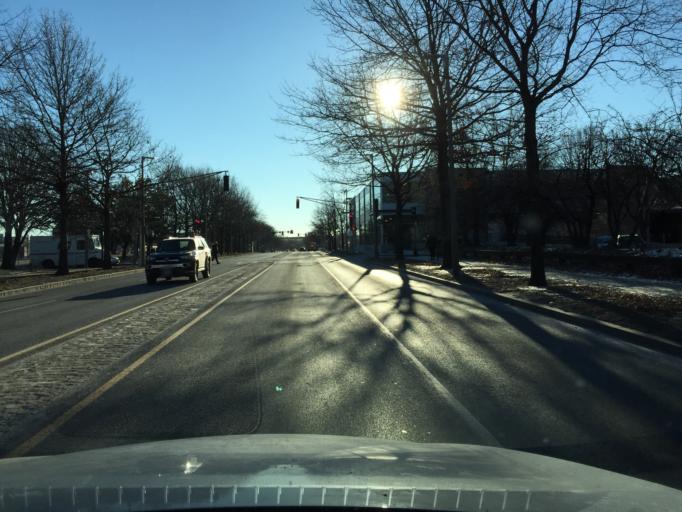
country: US
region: Massachusetts
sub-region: Suffolk County
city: South Boston
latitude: 42.3340
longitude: -71.0831
